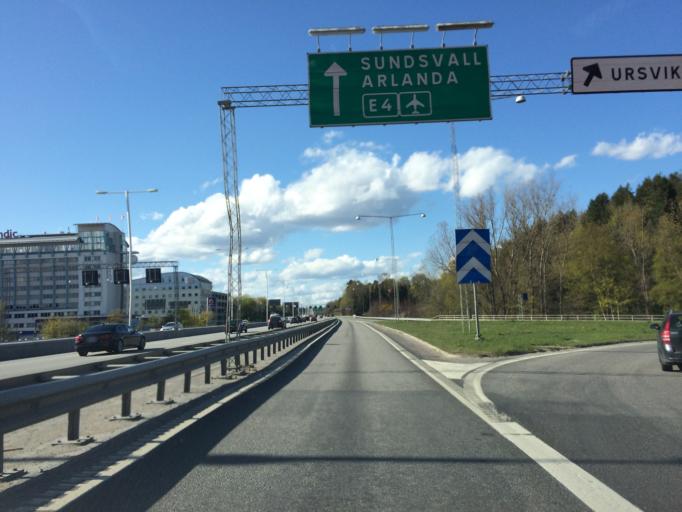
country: SE
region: Stockholm
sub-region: Norrtalje Kommun
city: Bergshamra
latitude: 59.3787
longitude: 18.0129
